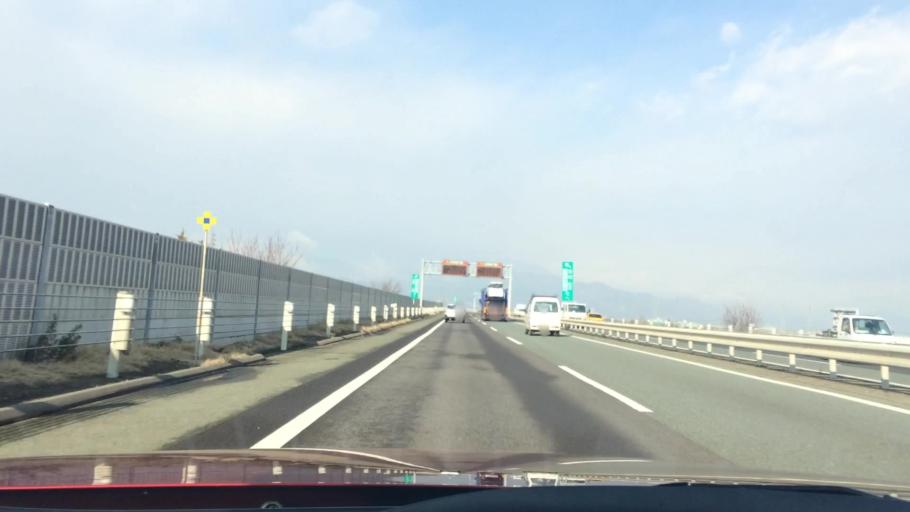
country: JP
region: Nagano
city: Nagano-shi
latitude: 36.5429
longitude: 138.1393
